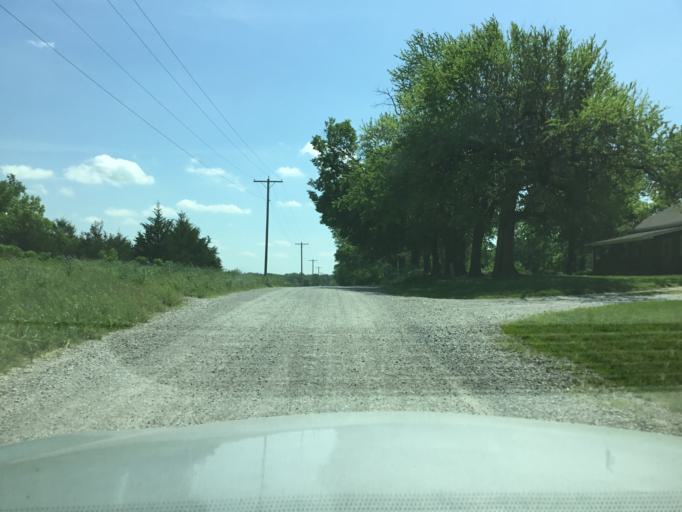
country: US
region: Kansas
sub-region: Labette County
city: Parsons
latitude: 37.3110
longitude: -95.2565
